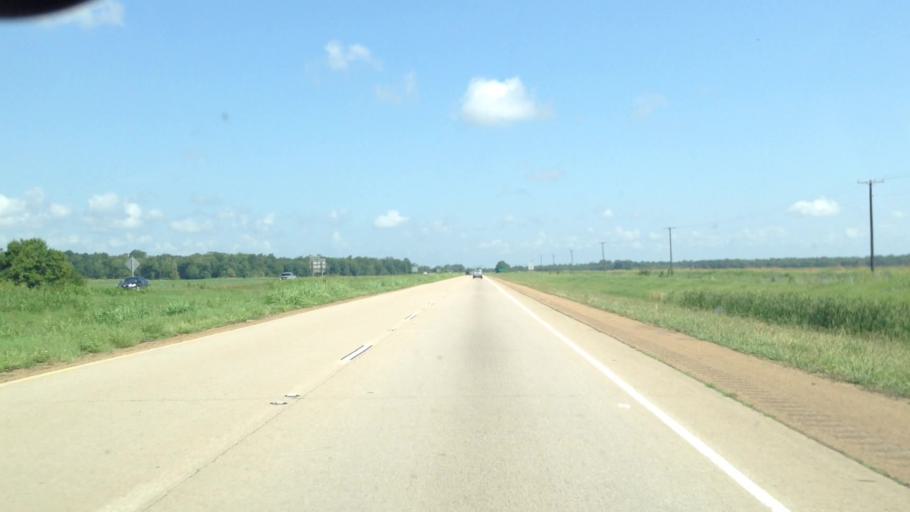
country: US
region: Louisiana
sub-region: Rapides Parish
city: Woodworth
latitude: 31.1734
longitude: -92.4645
